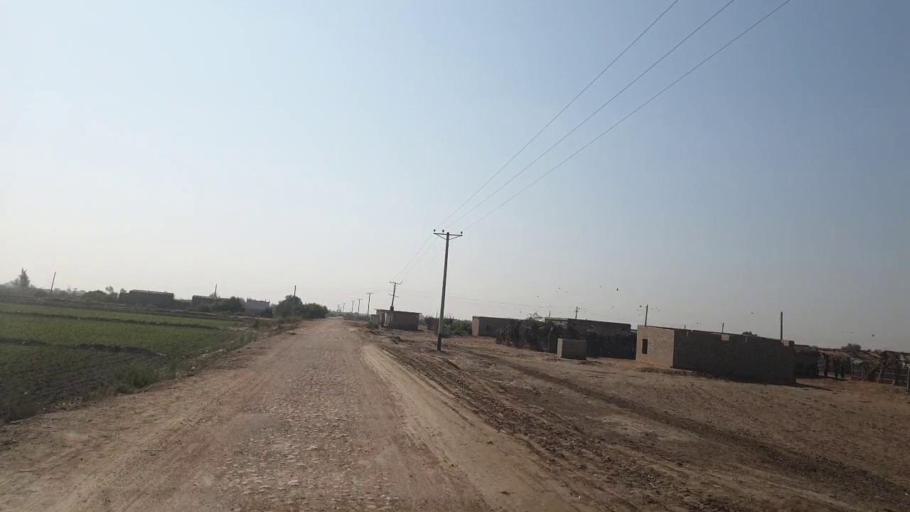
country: PK
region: Sindh
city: Thatta
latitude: 24.7324
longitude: 67.7942
